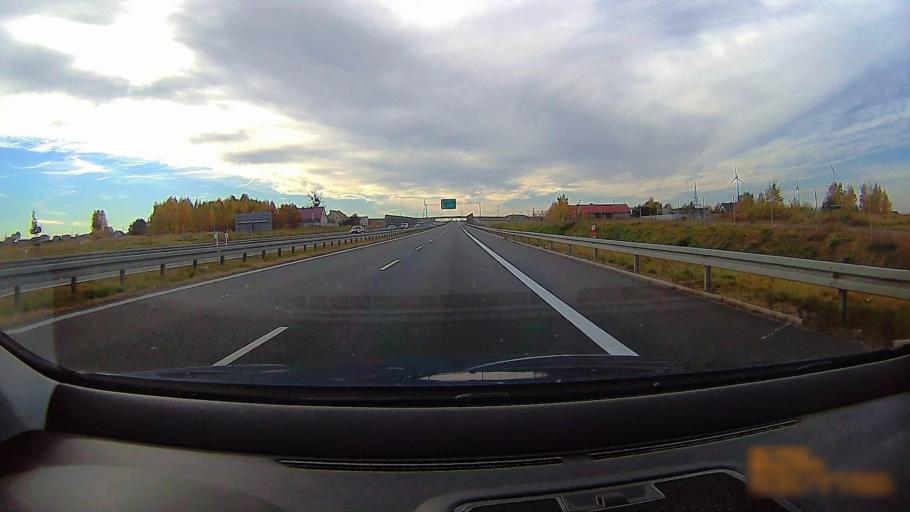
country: PL
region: Greater Poland Voivodeship
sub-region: Powiat ostrowski
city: Przygodzice
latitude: 51.6370
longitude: 17.8738
